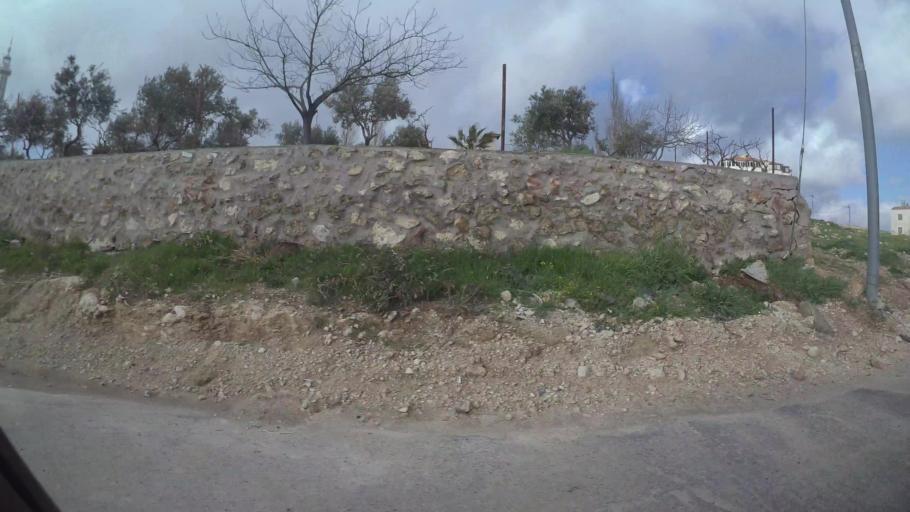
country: JO
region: Amman
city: Al Jubayhah
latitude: 32.0542
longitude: 35.8923
